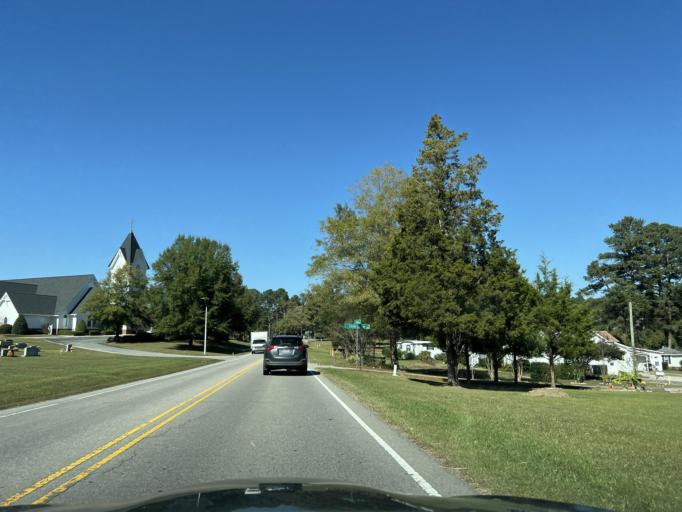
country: US
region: North Carolina
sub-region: Johnston County
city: Clayton
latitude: 35.6843
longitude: -78.5263
